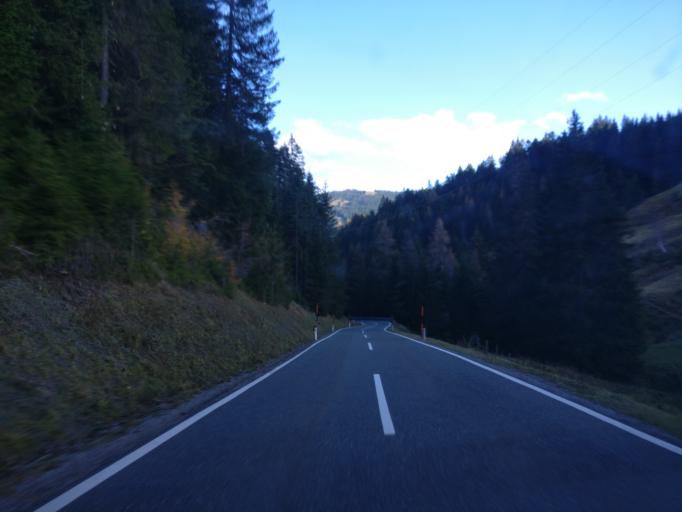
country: AT
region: Salzburg
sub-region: Politischer Bezirk Zell am See
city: Dienten am Hochkonig
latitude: 47.3966
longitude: 13.0070
